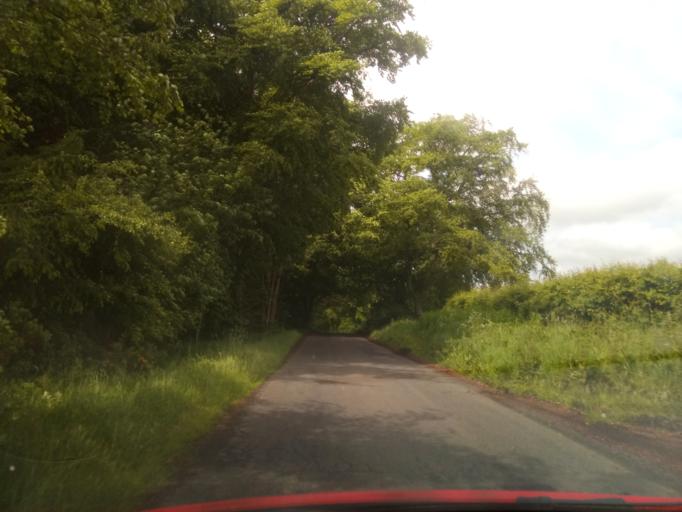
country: GB
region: Scotland
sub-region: The Scottish Borders
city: Selkirk
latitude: 55.5141
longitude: -2.8024
